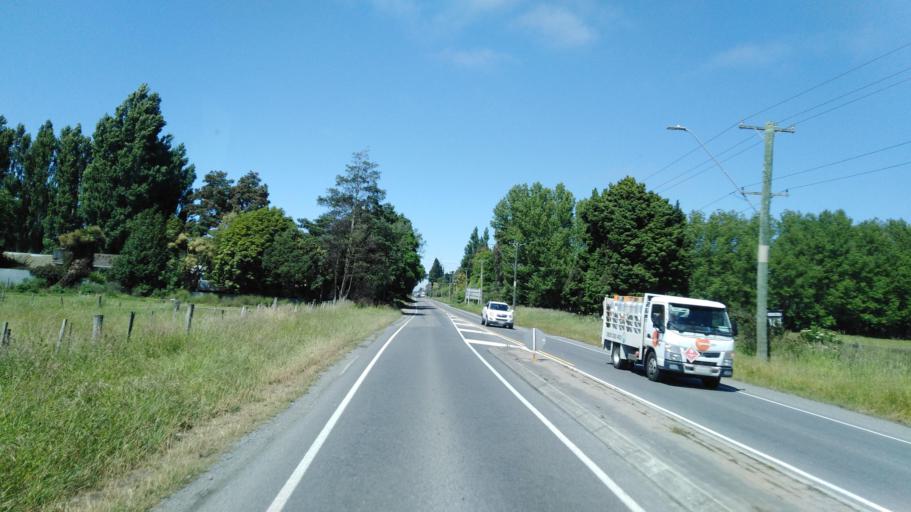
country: NZ
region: Canterbury
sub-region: Selwyn District
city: Prebbleton
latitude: -43.5200
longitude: 172.5047
